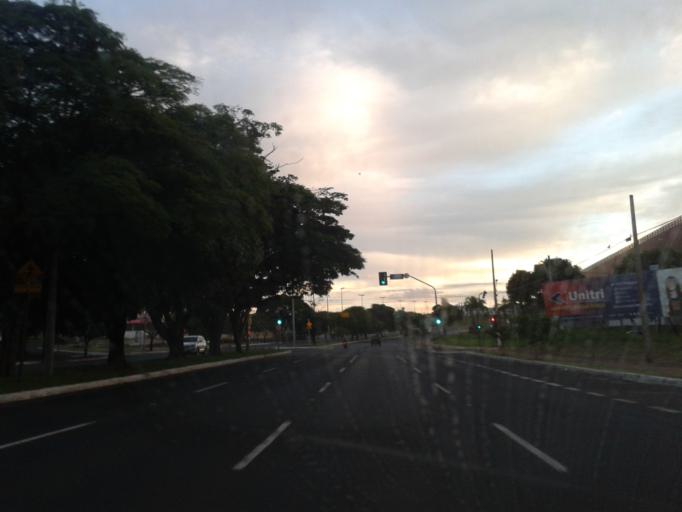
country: BR
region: Minas Gerais
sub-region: Uberlandia
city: Uberlandia
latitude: -18.8967
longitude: -48.2555
